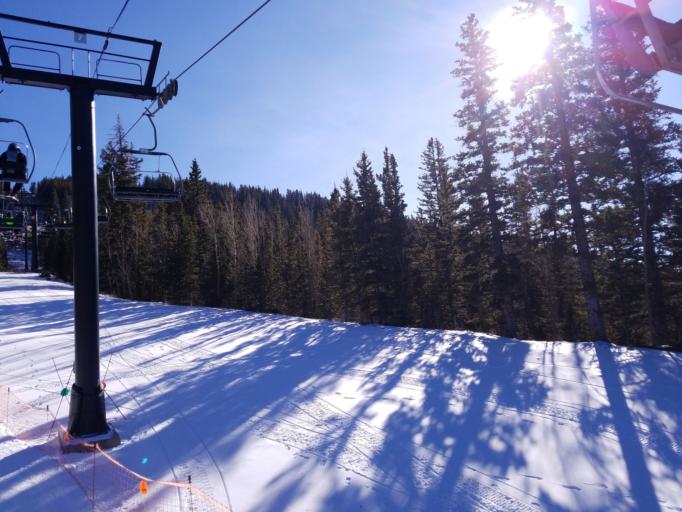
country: US
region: New Mexico
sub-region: Santa Fe County
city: Santa Fe
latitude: 35.7913
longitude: -105.7992
